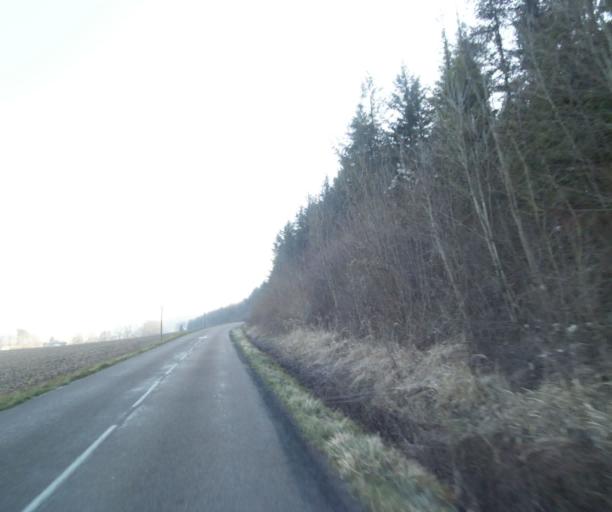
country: FR
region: Champagne-Ardenne
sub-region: Departement de la Haute-Marne
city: Bienville
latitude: 48.5628
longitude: 5.0818
